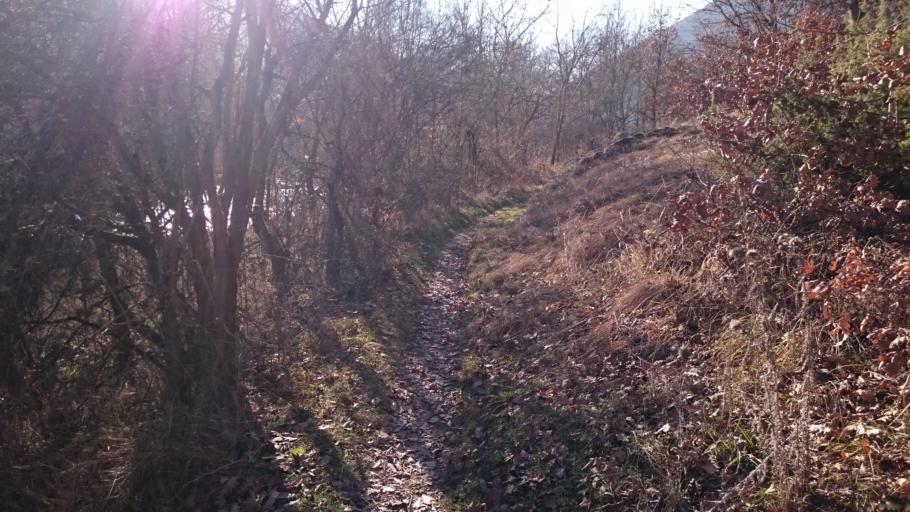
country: MK
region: Makedonski Brod
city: Makedonski Brod
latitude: 41.5118
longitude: 21.2274
